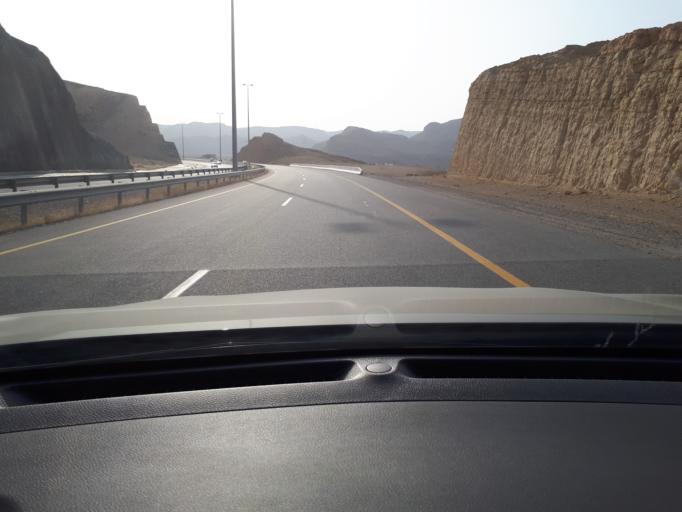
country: OM
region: Muhafazat Masqat
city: Muscat
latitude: 23.2090
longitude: 58.8939
